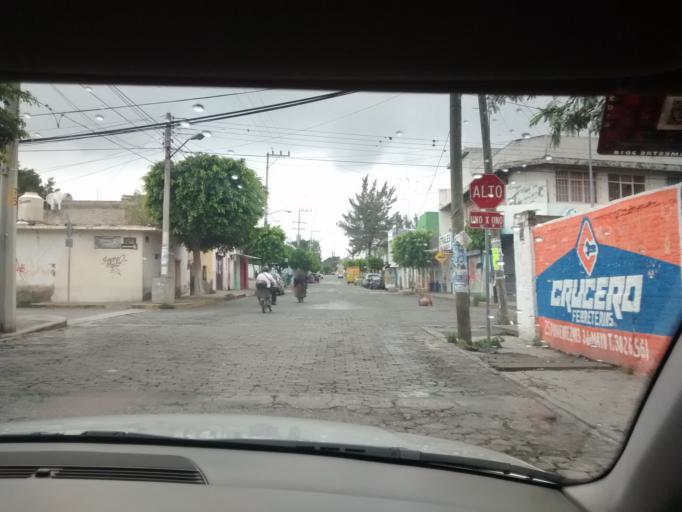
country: MX
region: Puebla
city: Tehuacan
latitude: 18.4569
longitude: -97.3985
